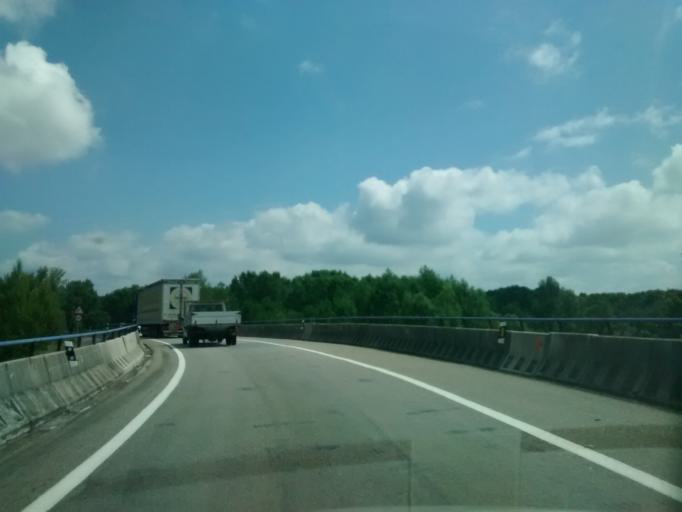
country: ES
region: Castille and Leon
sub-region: Provincia de Leon
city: Carracedelo
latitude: 42.5682
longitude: -6.7428
